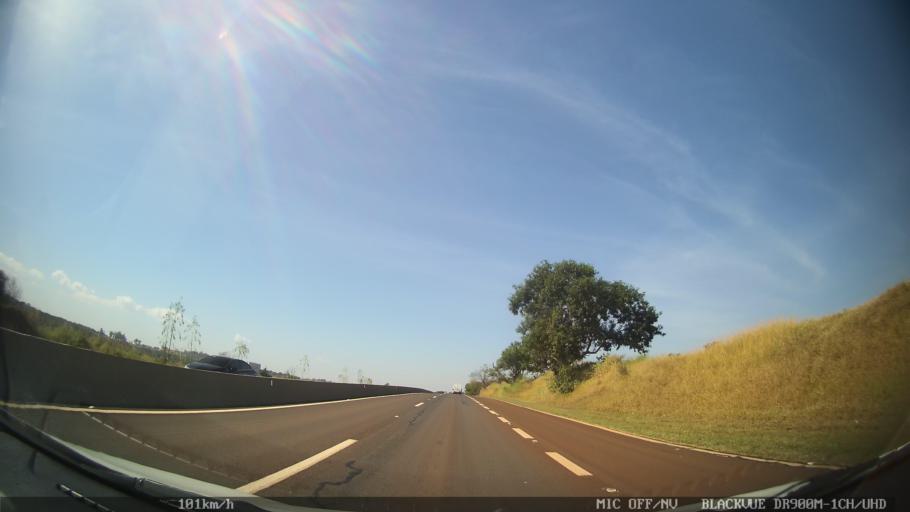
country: BR
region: Sao Paulo
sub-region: Ribeirao Preto
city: Ribeirao Preto
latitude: -21.1669
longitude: -47.8731
